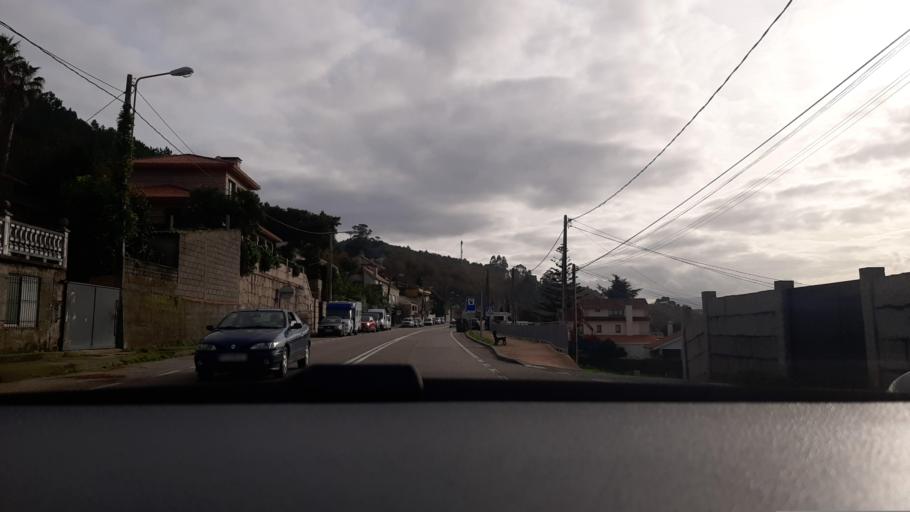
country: ES
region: Galicia
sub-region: Provincia de Pontevedra
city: Nigran
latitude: 42.1764
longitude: -8.7998
